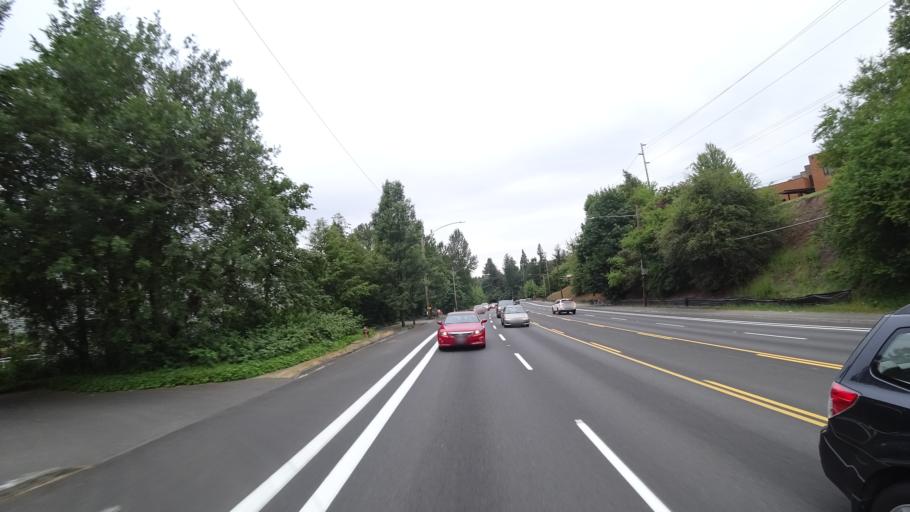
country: US
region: Oregon
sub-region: Multnomah County
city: Portland
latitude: 45.4806
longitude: -122.7053
